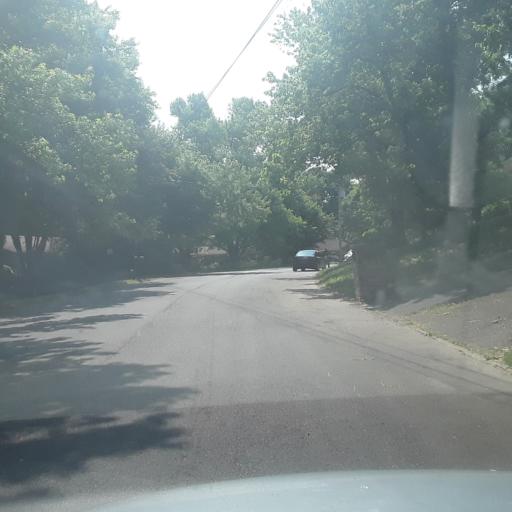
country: US
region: Tennessee
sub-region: Williamson County
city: Brentwood Estates
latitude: 36.0374
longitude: -86.7086
